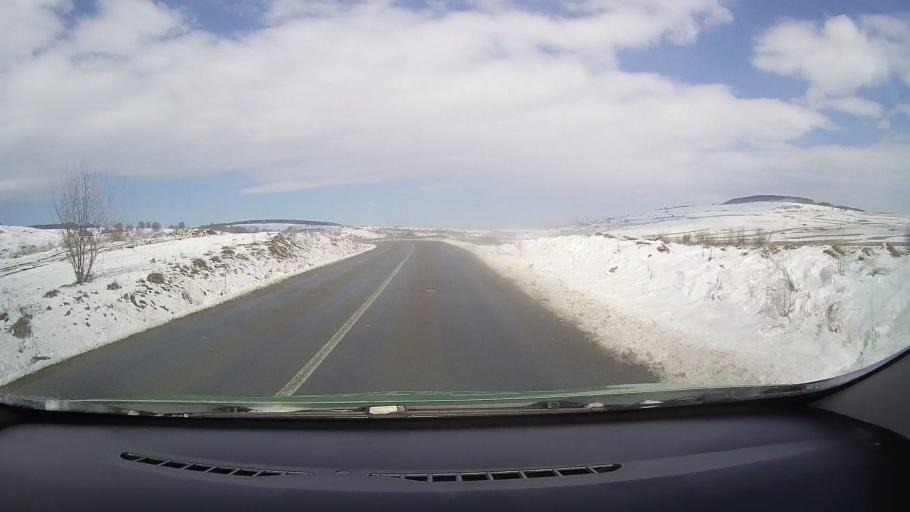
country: RO
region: Sibiu
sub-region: Comuna Altina
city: Altina
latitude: 45.9413
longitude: 24.4539
